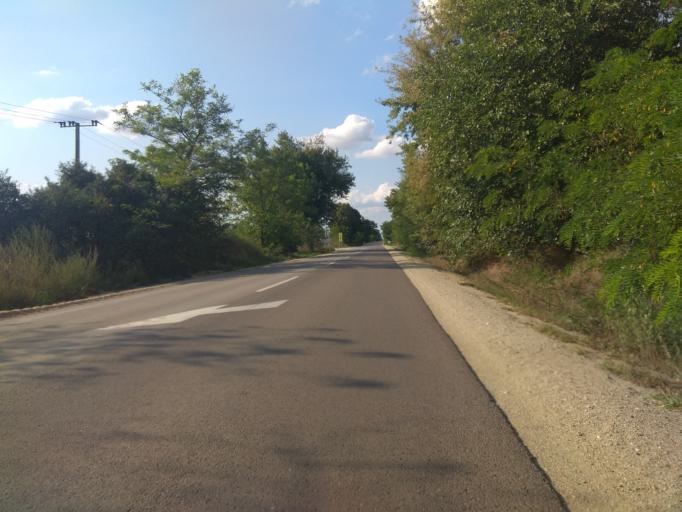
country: HU
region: Borsod-Abauj-Zemplen
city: Hejobaba
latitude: 47.8928
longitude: 20.8941
